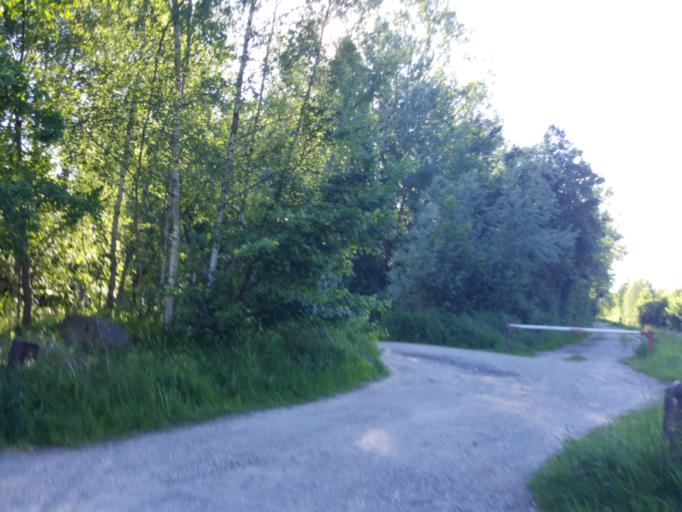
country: DE
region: Schleswig-Holstein
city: Oststeinbek
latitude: 53.5239
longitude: 10.1404
